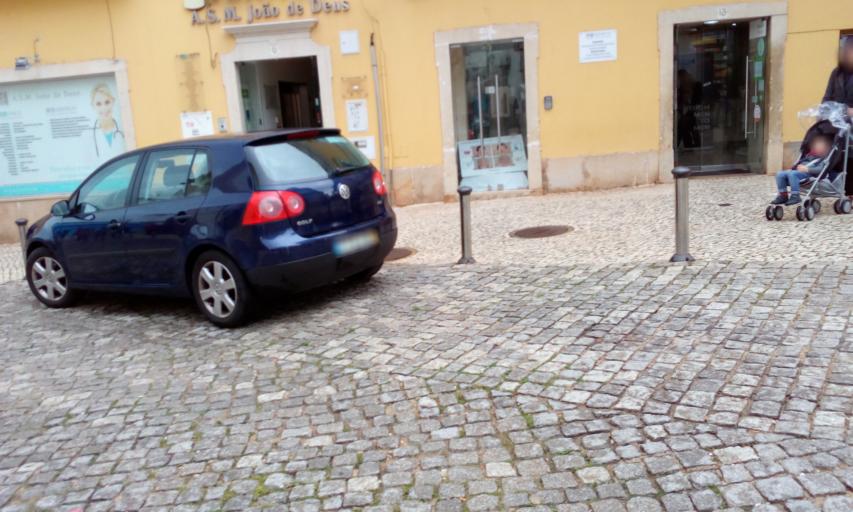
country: PT
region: Faro
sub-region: Silves
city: Silves
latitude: 37.1875
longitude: -8.4394
